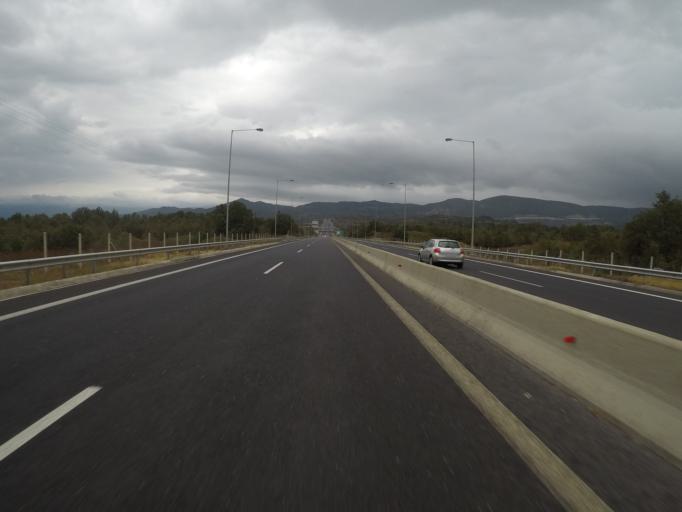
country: GR
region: Peloponnese
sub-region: Nomos Arkadias
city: Megalopoli
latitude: 37.3742
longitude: 22.1591
